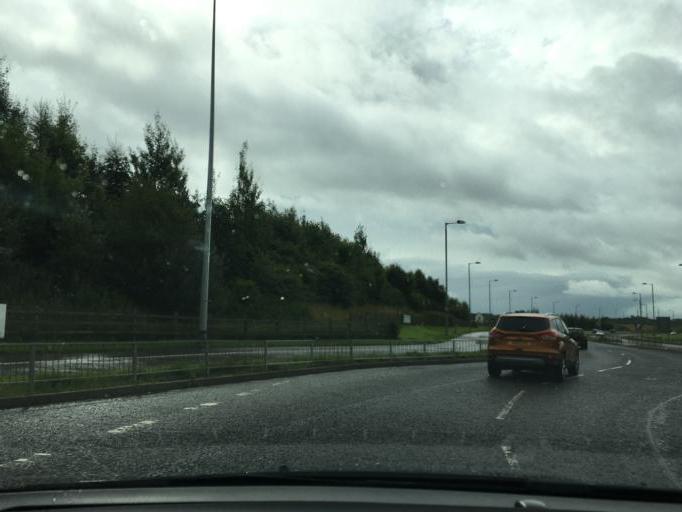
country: GB
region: Scotland
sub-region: North Lanarkshire
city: Holytown
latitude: 55.7999
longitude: -3.9613
